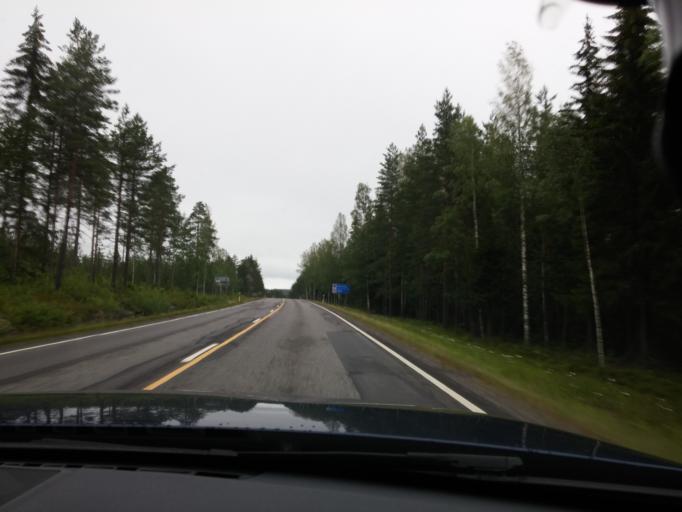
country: FI
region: Pirkanmaa
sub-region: Ylae-Pirkanmaa
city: Vilppula
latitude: 61.9088
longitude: 24.5257
